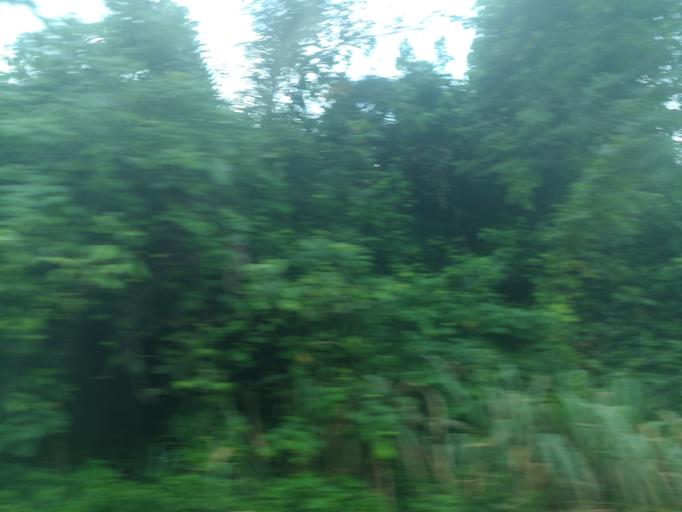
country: NG
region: Lagos
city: Ikorodu
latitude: 6.6653
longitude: 3.6379
